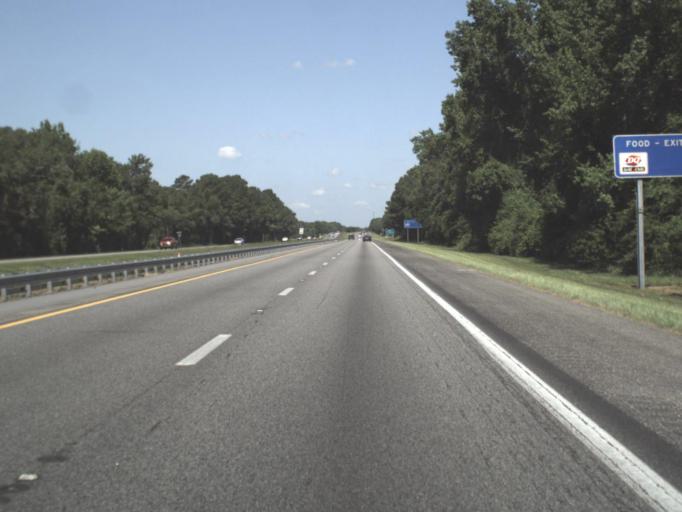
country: US
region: Florida
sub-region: Madison County
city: Madison
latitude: 30.4321
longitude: -83.6148
